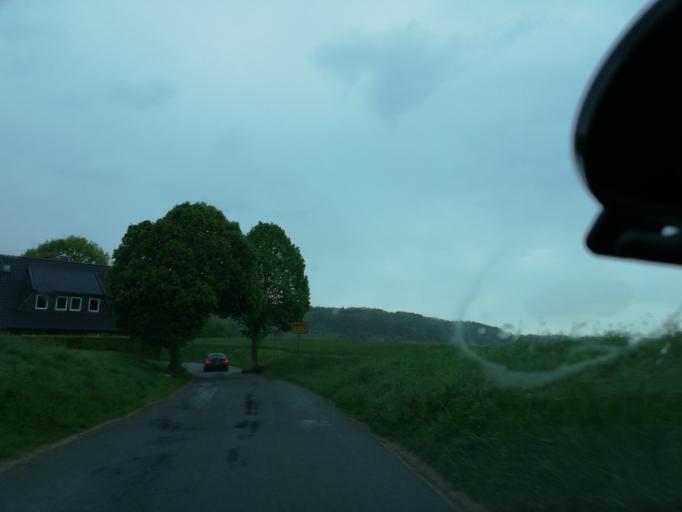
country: DE
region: Lower Saxony
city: Rinteln
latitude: 52.1220
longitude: 9.0721
